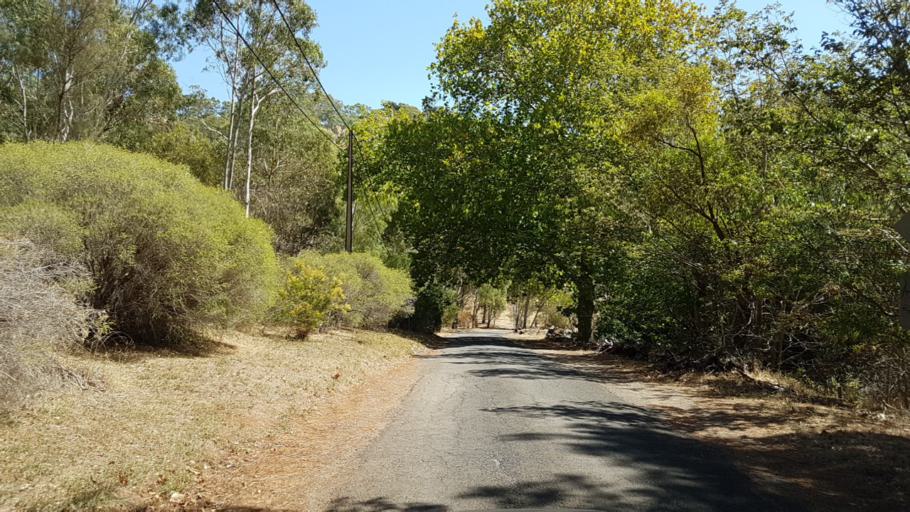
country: AU
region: South Australia
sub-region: Burnside
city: Mount Osmond
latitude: -34.9891
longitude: 138.6491
